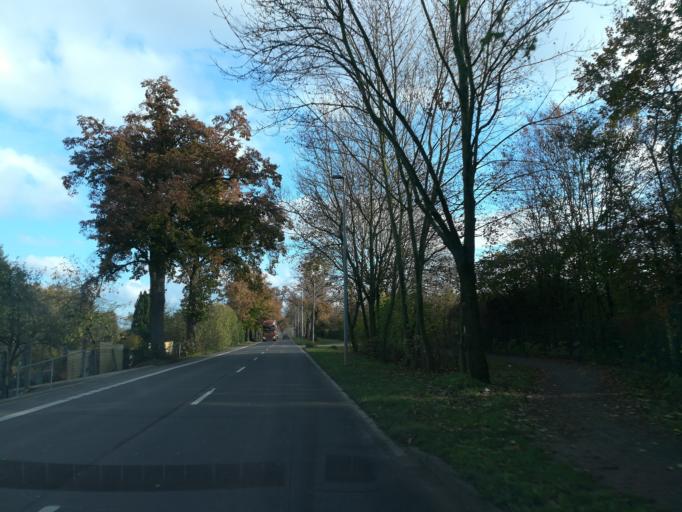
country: DE
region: Saxony-Anhalt
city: Haldensleben I
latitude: 52.2852
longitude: 11.4242
